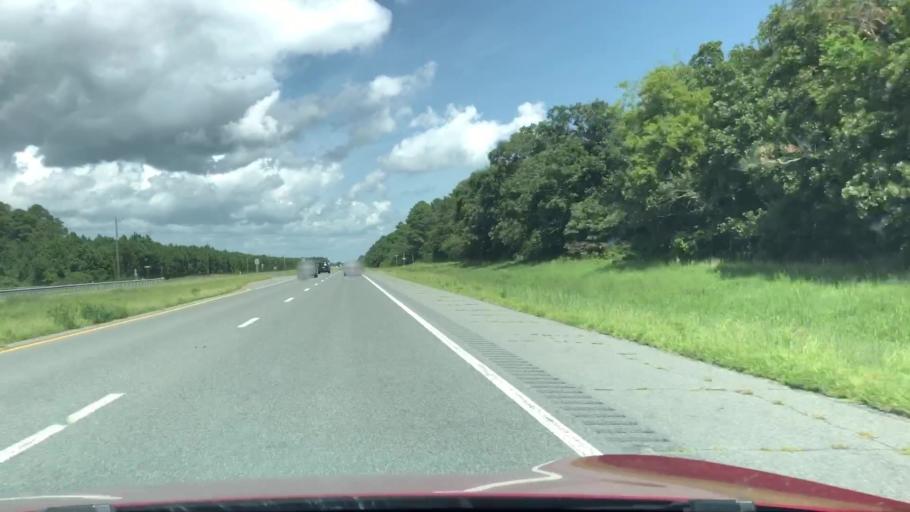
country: US
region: Virginia
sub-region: Northampton County
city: Cape Charles
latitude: 37.1538
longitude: -75.9712
